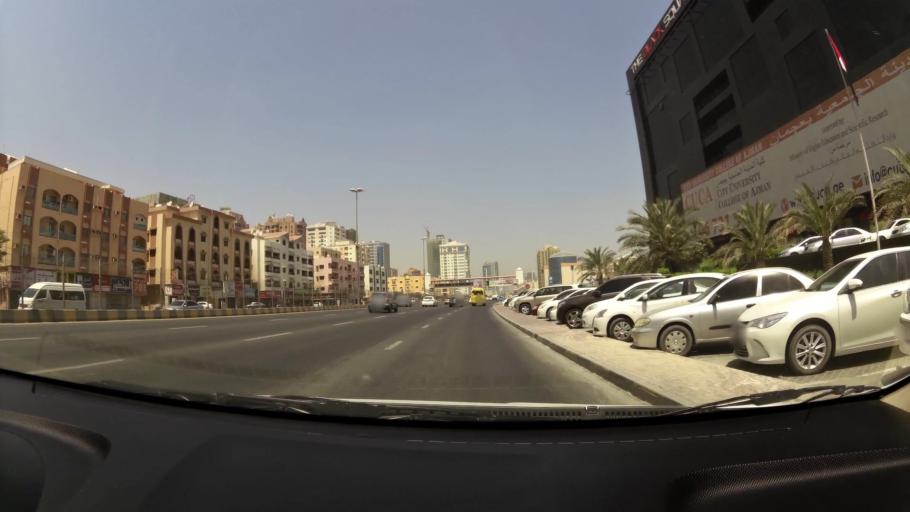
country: AE
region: Ajman
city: Ajman
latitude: 25.3889
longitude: 55.4625
